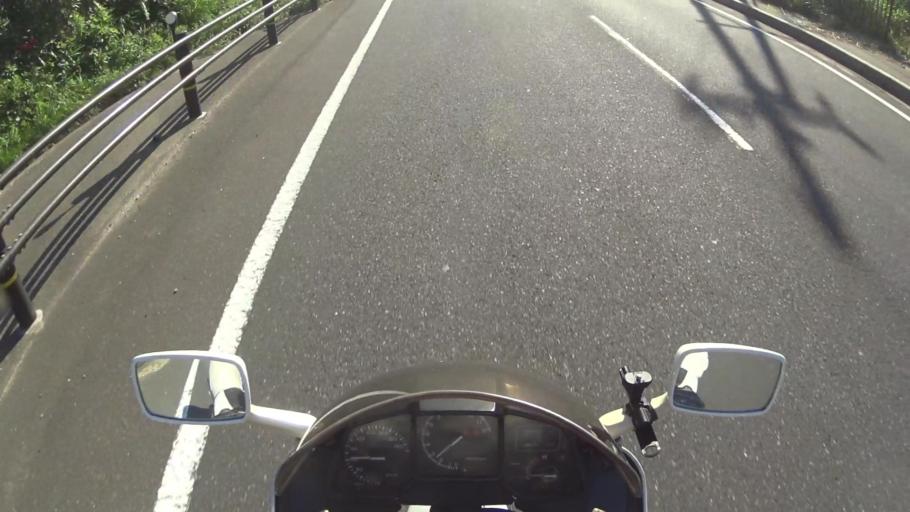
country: JP
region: Hyogo
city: Toyooka
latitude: 35.6457
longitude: 134.9497
